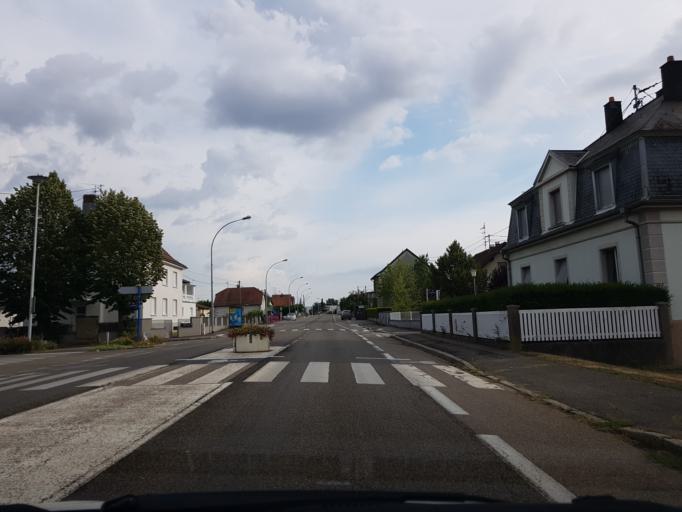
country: FR
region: Alsace
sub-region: Departement du Haut-Rhin
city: Wittenheim
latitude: 47.8195
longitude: 7.3395
